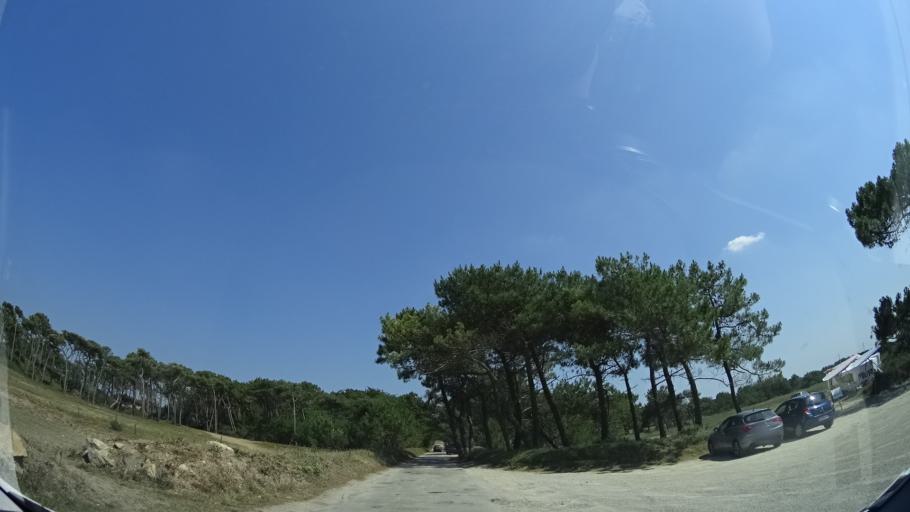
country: FR
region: Brittany
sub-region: Departement du Morbihan
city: Plouharnel
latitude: 47.5941
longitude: -3.1358
